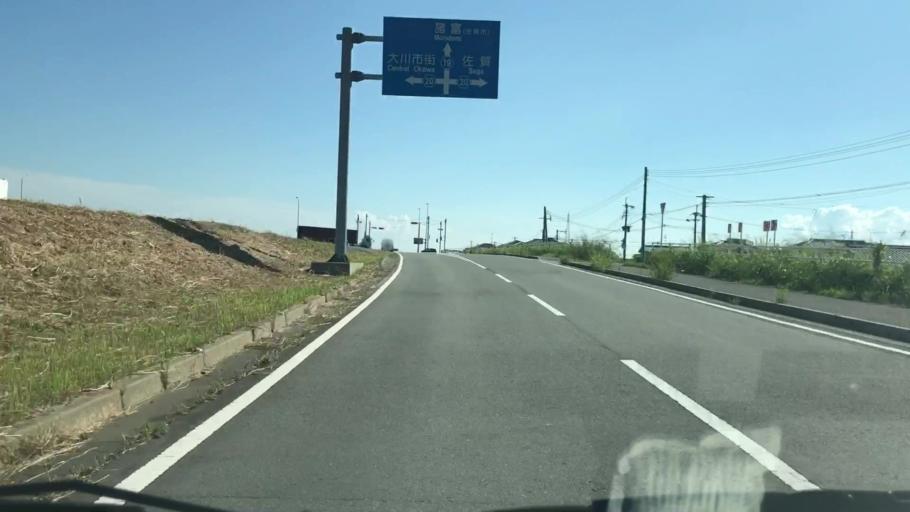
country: JP
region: Saga Prefecture
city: Okawa
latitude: 33.2378
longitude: 130.3806
